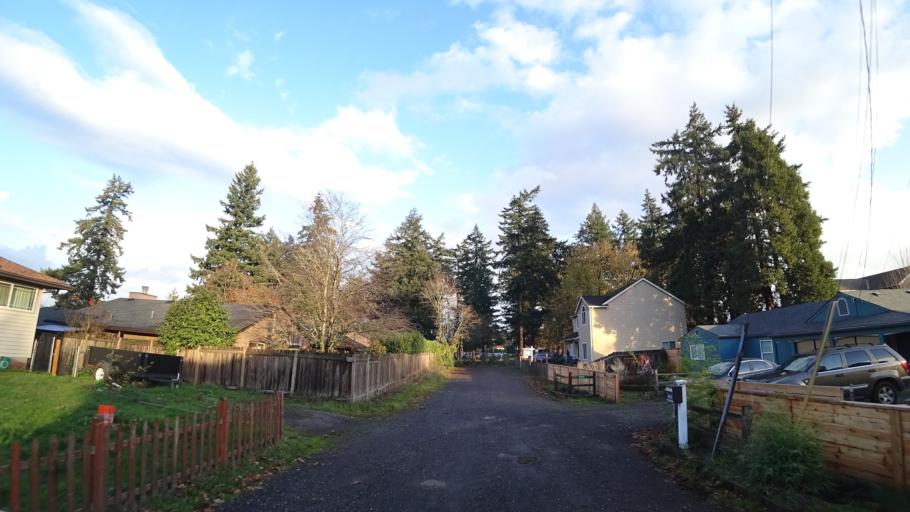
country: US
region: Oregon
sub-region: Multnomah County
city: Lents
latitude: 45.5162
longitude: -122.5408
